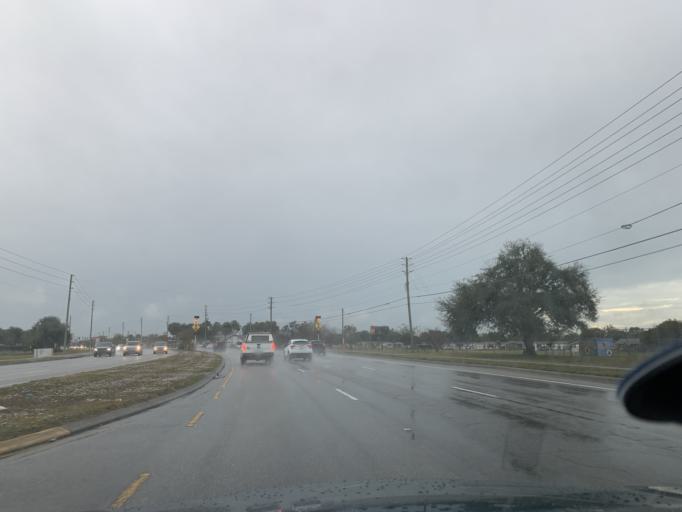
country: US
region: Florida
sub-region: Pasco County
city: Jasmine Estates
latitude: 28.2948
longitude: -82.6755
